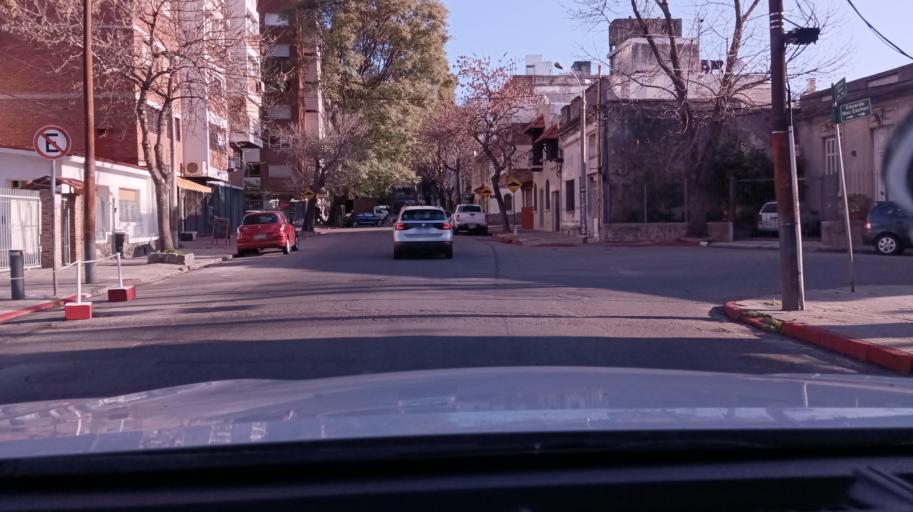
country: UY
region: Montevideo
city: Montevideo
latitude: -34.9054
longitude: -56.1495
